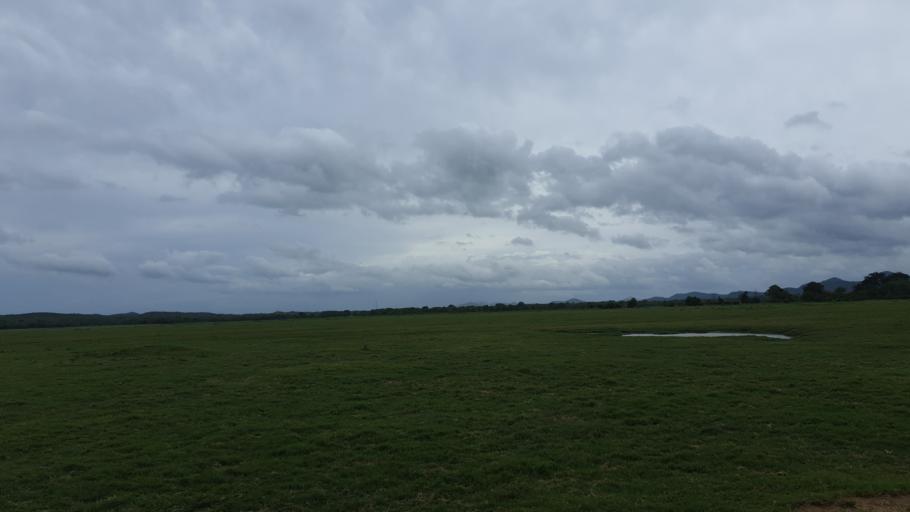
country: LK
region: North Central
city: Polonnaruwa
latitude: 8.1302
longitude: 80.9063
